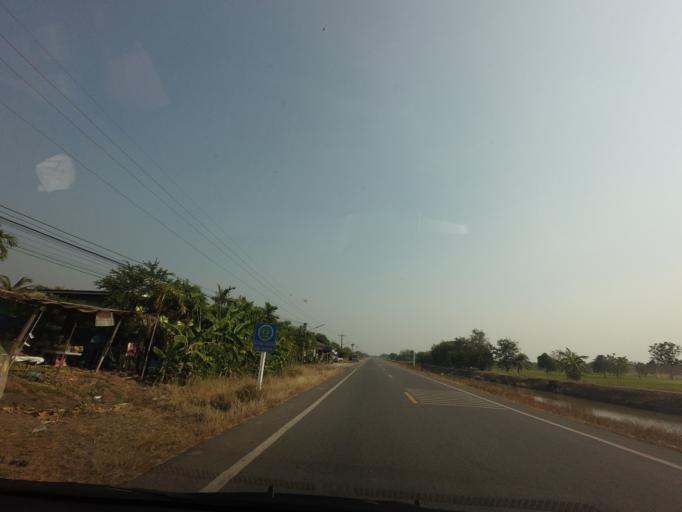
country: TH
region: Chachoengsao
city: Khlong Khuean
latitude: 13.8082
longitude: 101.1701
